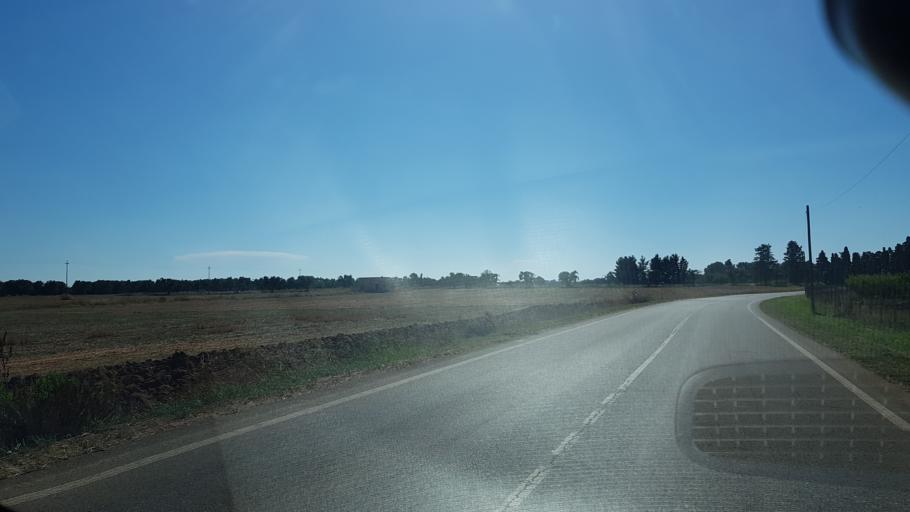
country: IT
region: Apulia
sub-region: Provincia di Brindisi
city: Mesagne
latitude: 40.5570
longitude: 17.8501
